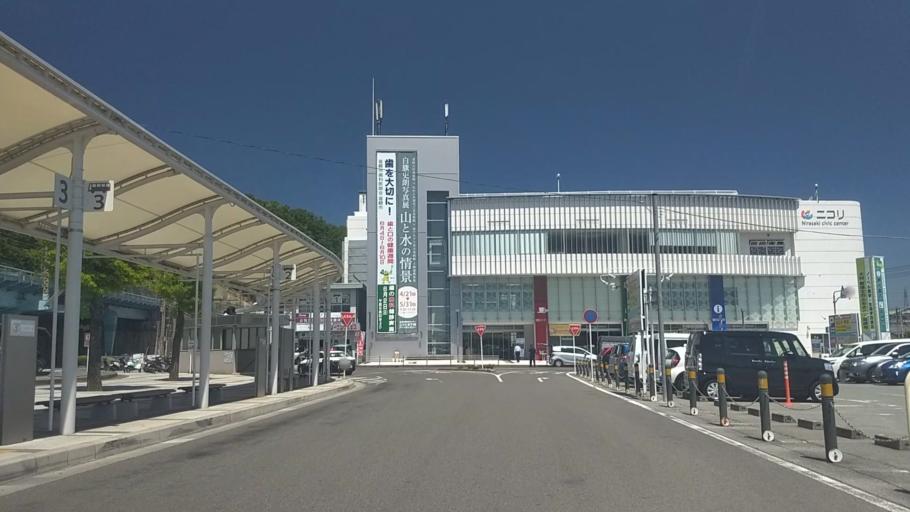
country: JP
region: Yamanashi
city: Nirasaki
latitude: 35.7109
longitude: 138.4506
